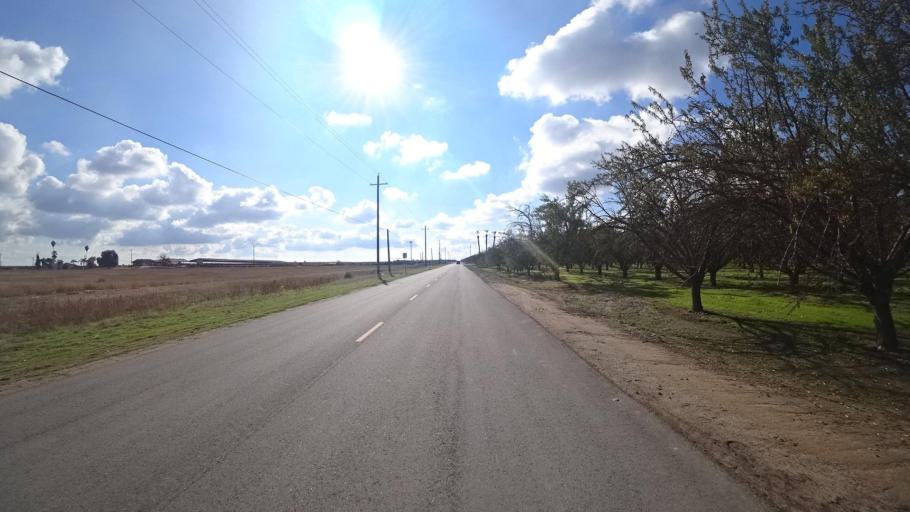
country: US
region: California
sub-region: Kern County
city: McFarland
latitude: 35.6619
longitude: -119.2410
